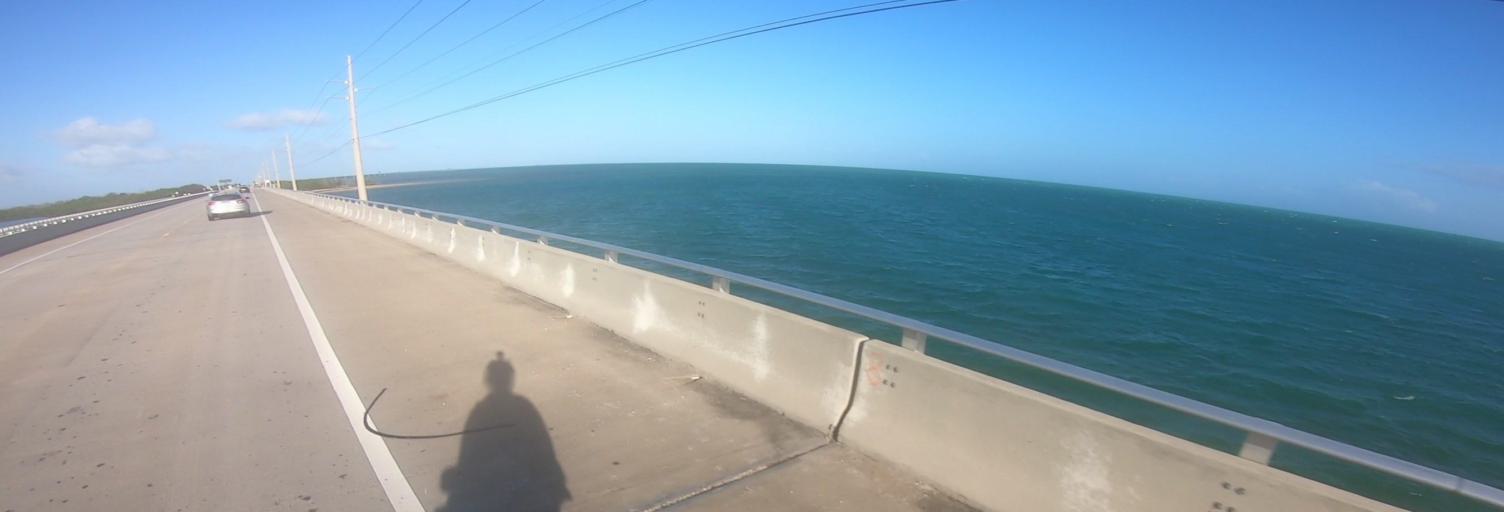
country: US
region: Florida
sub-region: Monroe County
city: Big Pine Key
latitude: 24.6747
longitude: -81.2422
